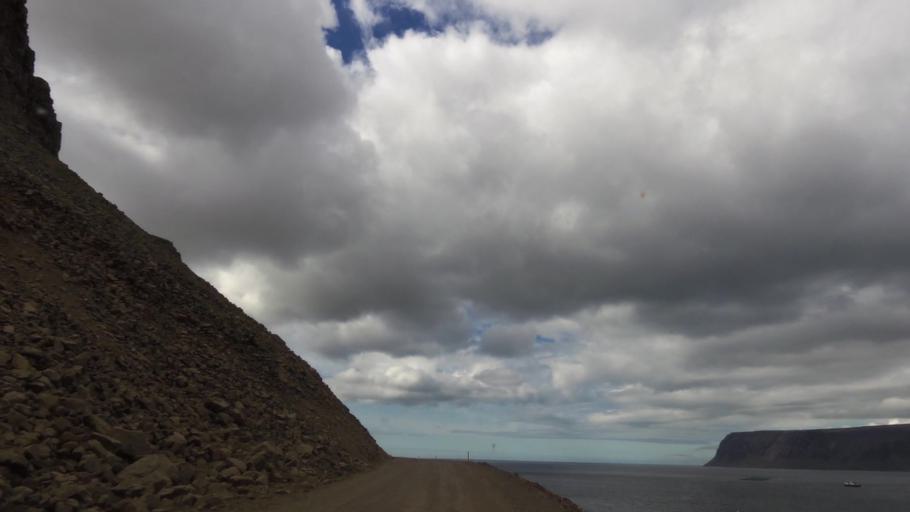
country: IS
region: West
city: Olafsvik
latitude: 65.5637
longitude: -24.0377
